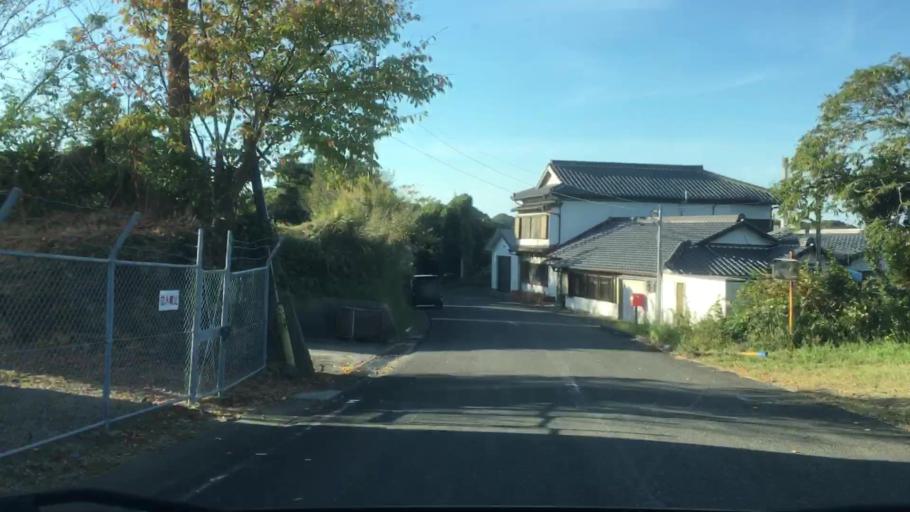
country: JP
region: Nagasaki
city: Sasebo
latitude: 33.0211
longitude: 129.5739
